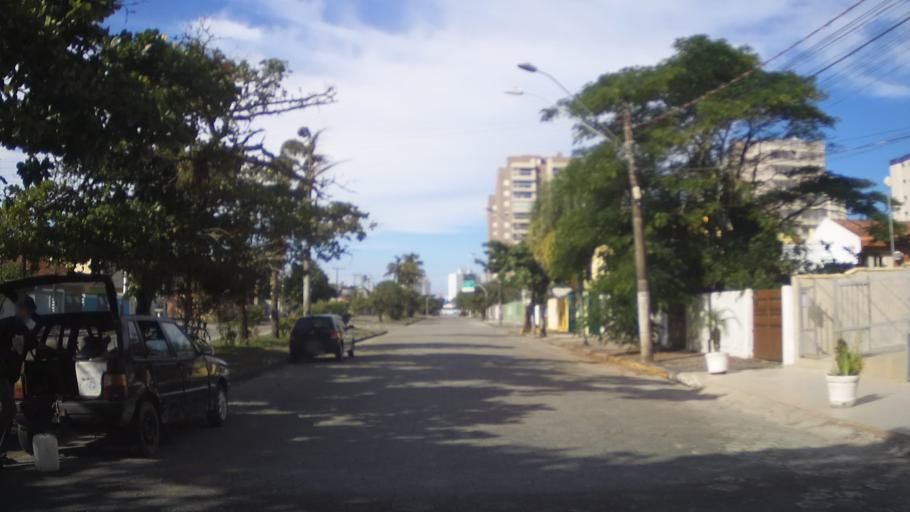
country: BR
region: Sao Paulo
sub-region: Itanhaem
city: Itanhaem
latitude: -24.1820
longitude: -46.7821
